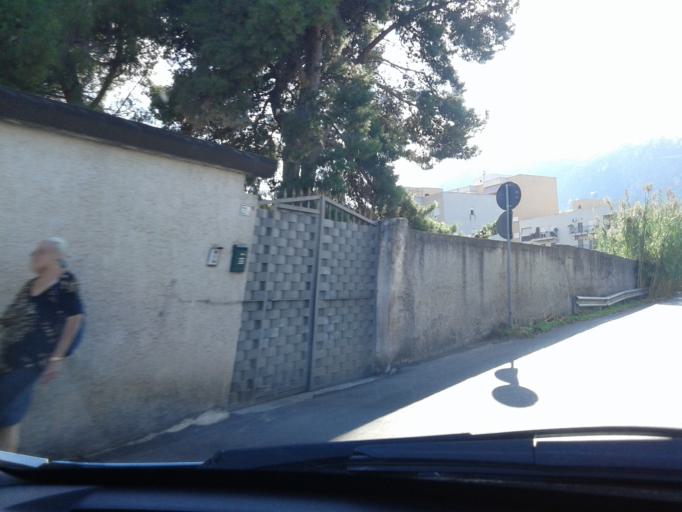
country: IT
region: Sicily
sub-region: Palermo
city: Palermo
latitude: 38.1035
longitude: 13.3187
